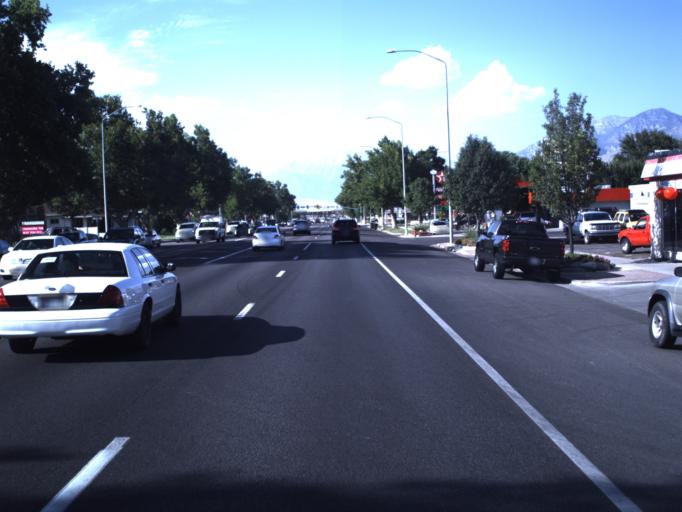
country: US
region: Utah
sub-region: Utah County
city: Spanish Fork
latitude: 40.1169
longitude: -111.6547
